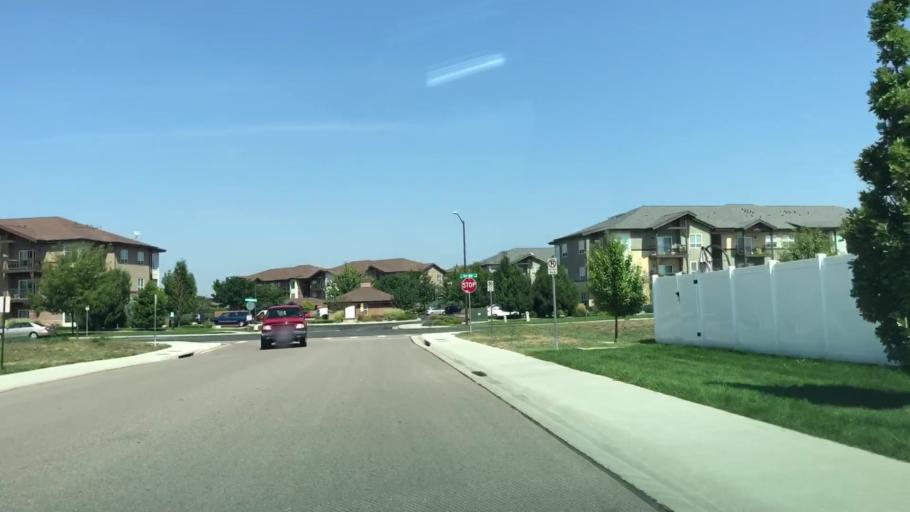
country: US
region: Colorado
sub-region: Larimer County
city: Loveland
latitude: 40.4026
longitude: -105.0343
